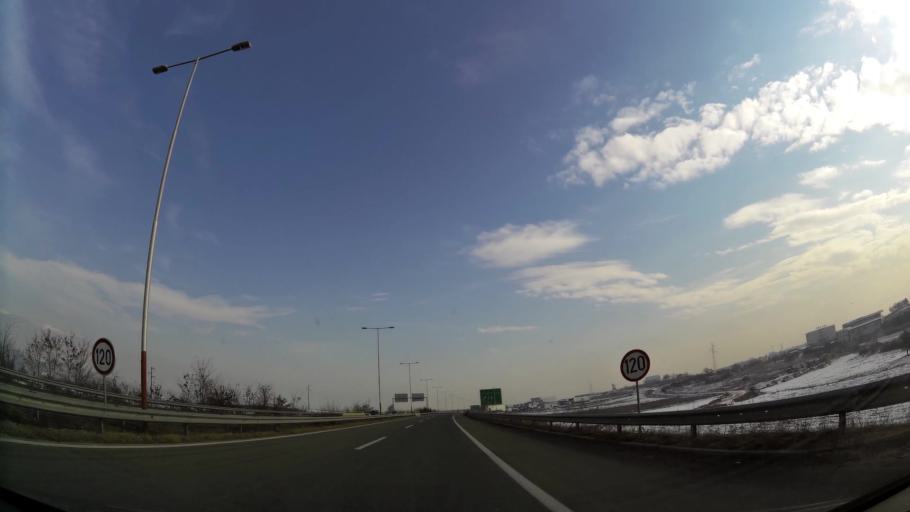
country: MK
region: Suto Orizari
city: Suto Orizare
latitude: 42.0519
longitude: 21.4254
